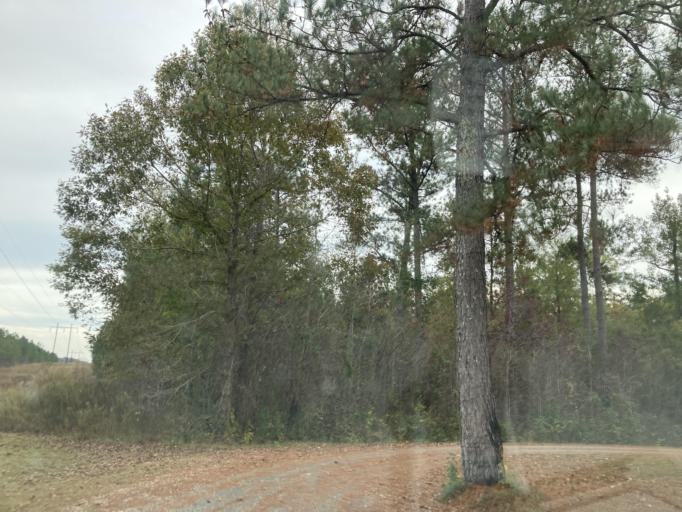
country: US
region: Mississippi
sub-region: Lamar County
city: Lumberton
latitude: 31.0564
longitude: -89.5144
